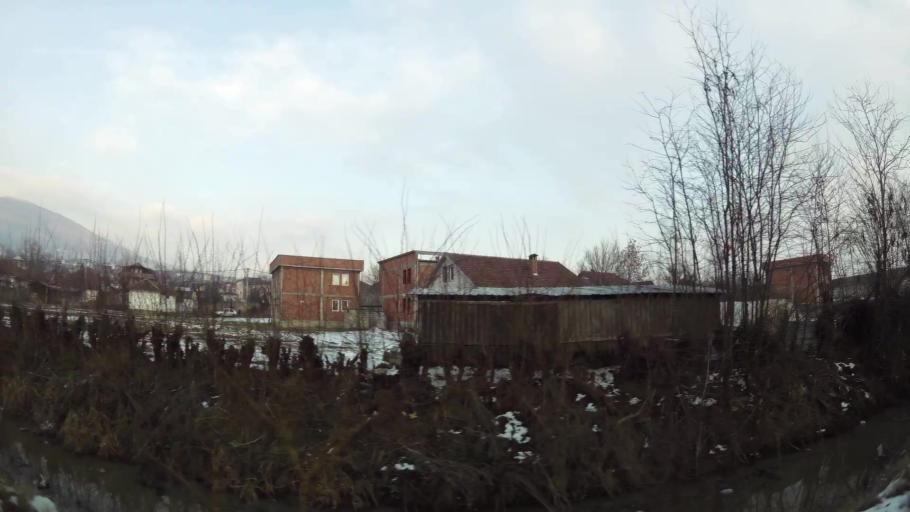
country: MK
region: Aracinovo
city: Arachinovo
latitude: 42.0218
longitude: 21.5593
